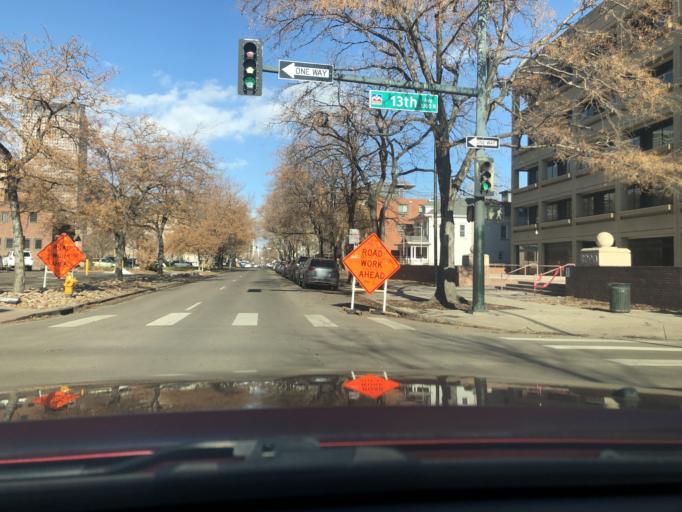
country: US
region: Colorado
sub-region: Denver County
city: Denver
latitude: 39.7368
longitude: -104.9823
